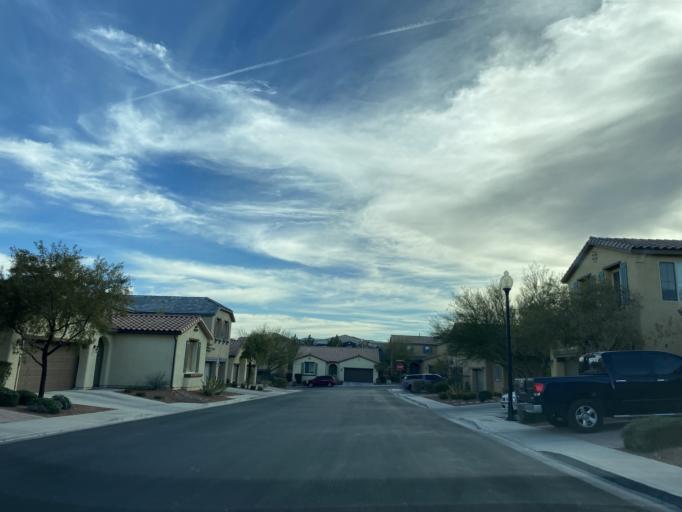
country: US
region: Nevada
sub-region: Clark County
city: Summerlin South
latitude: 36.2783
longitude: -115.3313
